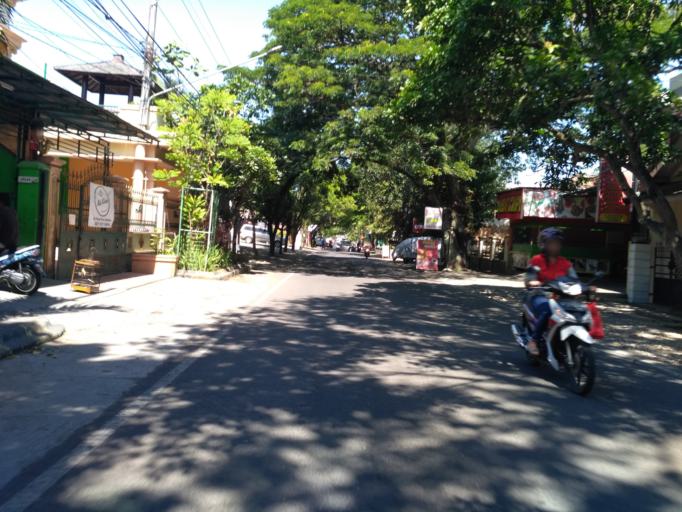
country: ID
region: East Java
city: Malang
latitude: -7.9785
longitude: 112.6638
